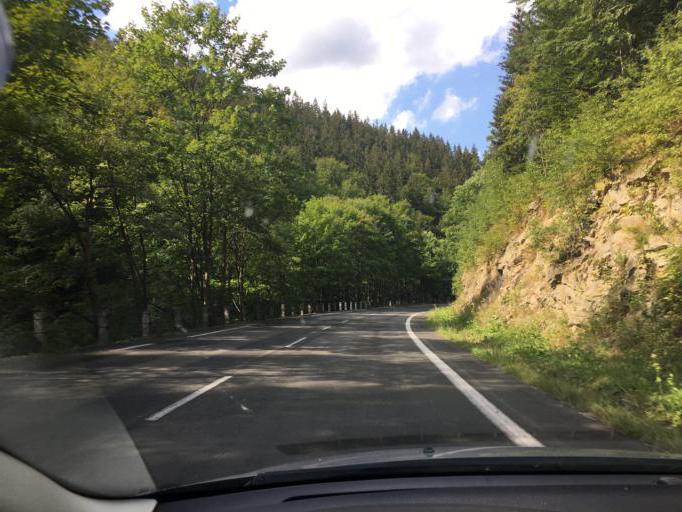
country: CZ
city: Benecko
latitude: 50.6750
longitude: 15.5929
